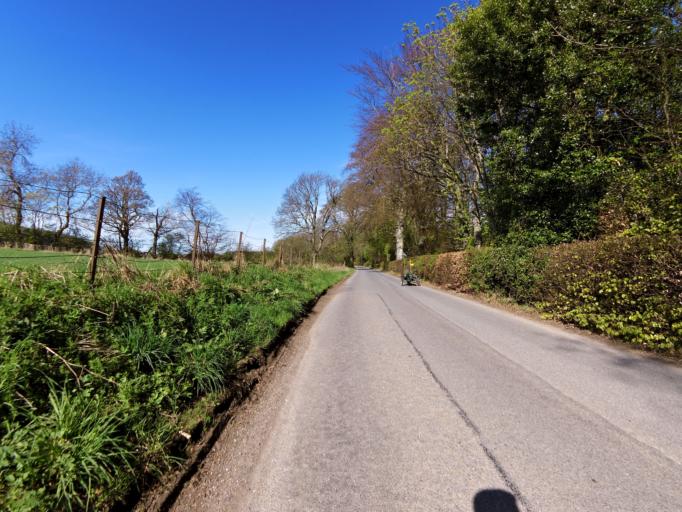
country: GB
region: Scotland
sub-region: Dundee City
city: Dundee
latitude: 56.4073
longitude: -3.0138
